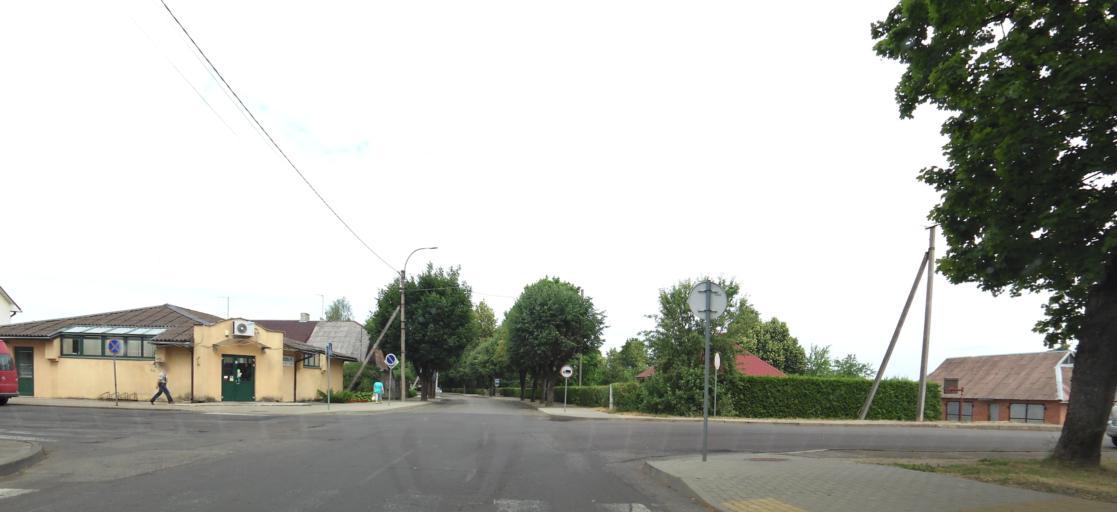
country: LT
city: Sirvintos
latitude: 55.0377
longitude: 24.9654
